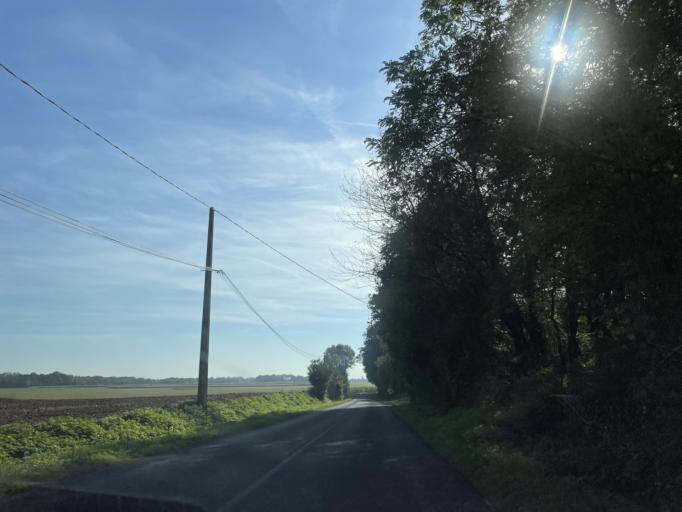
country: FR
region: Ile-de-France
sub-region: Departement de Seine-et-Marne
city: Saint-Jean-les-Deux-Jumeaux
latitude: 48.9120
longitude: 3.0181
